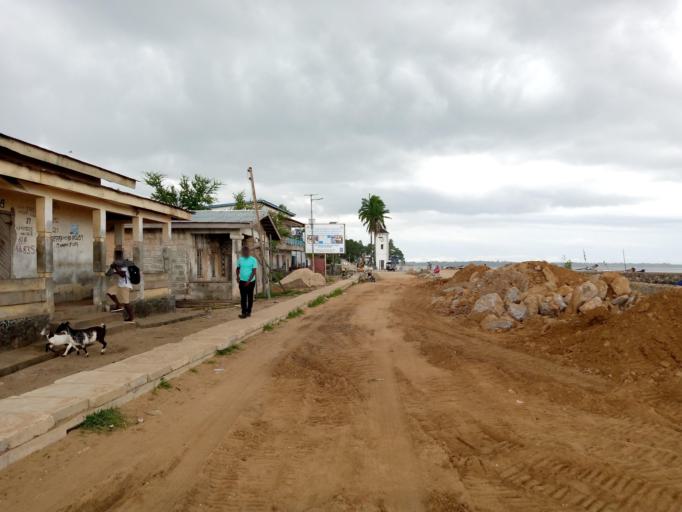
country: SL
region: Southern Province
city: Bonthe
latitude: 7.5296
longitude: -12.5010
